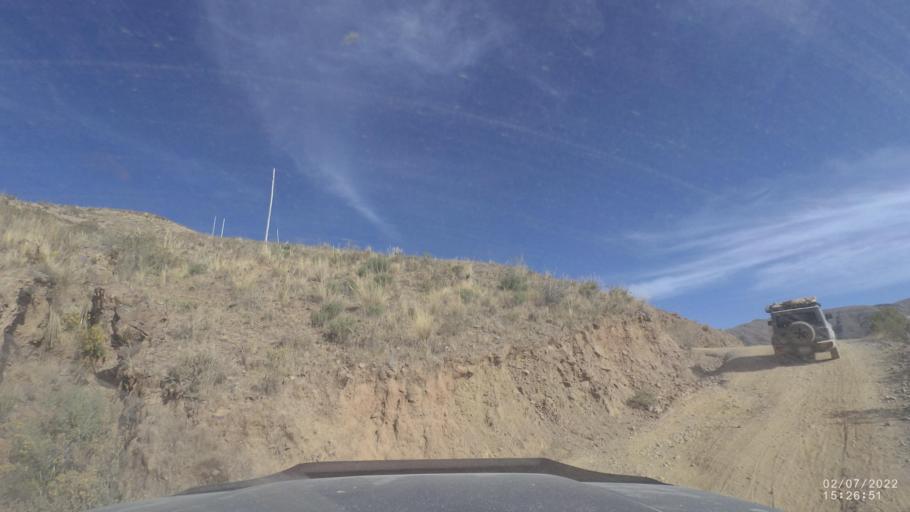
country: BO
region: Cochabamba
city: Irpa Irpa
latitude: -17.8782
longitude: -66.4152
